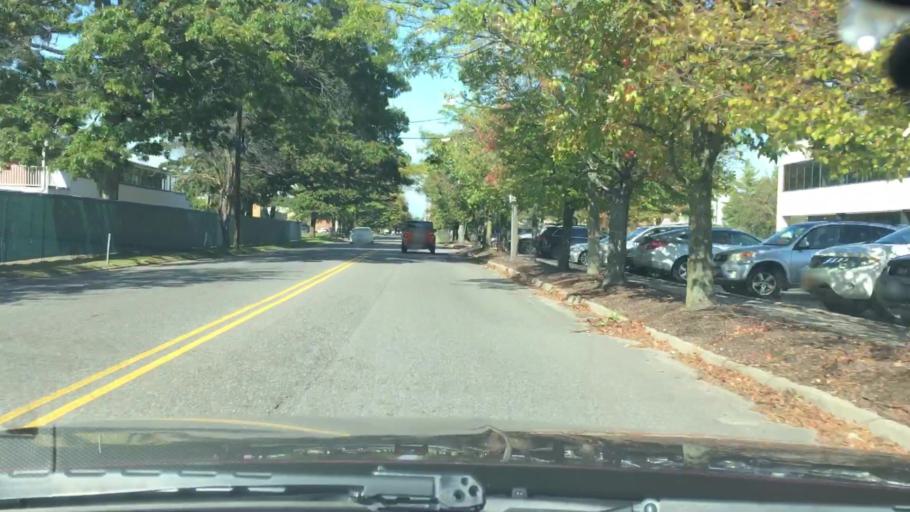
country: US
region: New York
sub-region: Suffolk County
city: Bohemia
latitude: 40.7889
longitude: -73.1379
